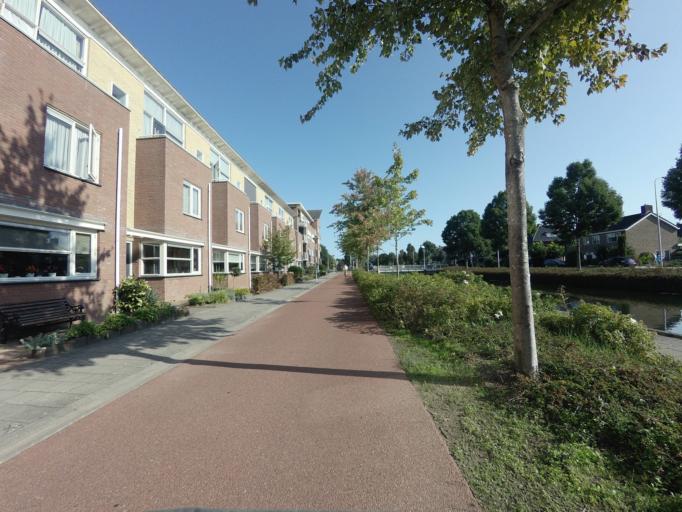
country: NL
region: Overijssel
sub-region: Gemeente Raalte
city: Raalte
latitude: 52.3847
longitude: 6.2796
